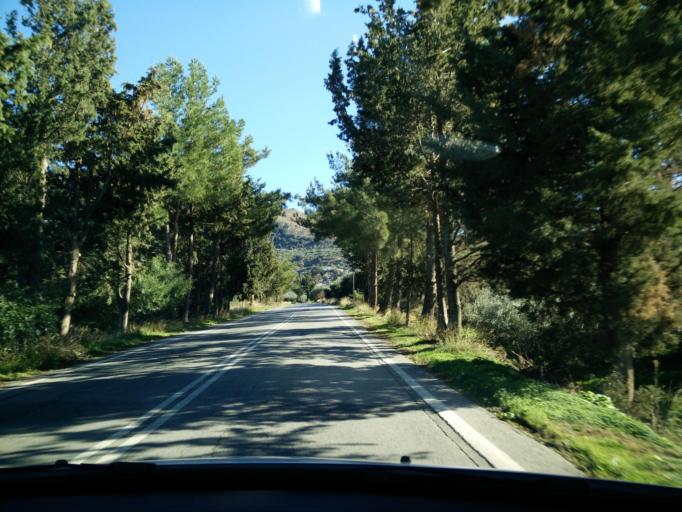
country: GR
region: Crete
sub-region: Nomos Irakleiou
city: Arkalochori
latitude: 35.0776
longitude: 25.3529
